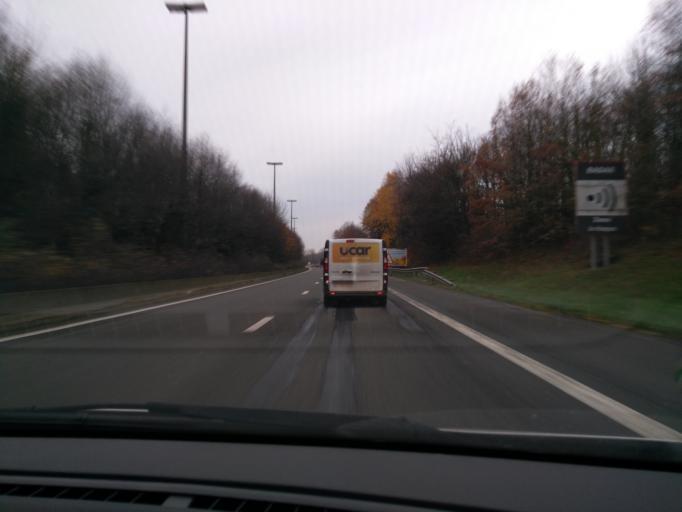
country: BE
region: Wallonia
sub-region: Province du Hainaut
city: Antoing
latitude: 50.5960
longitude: 3.4576
